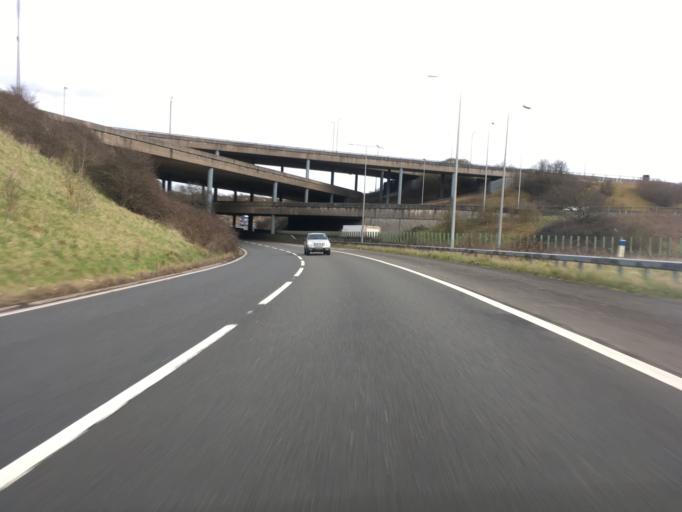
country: GB
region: England
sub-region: South Gloucestershire
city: Almondsbury
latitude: 51.5520
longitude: -2.5541
